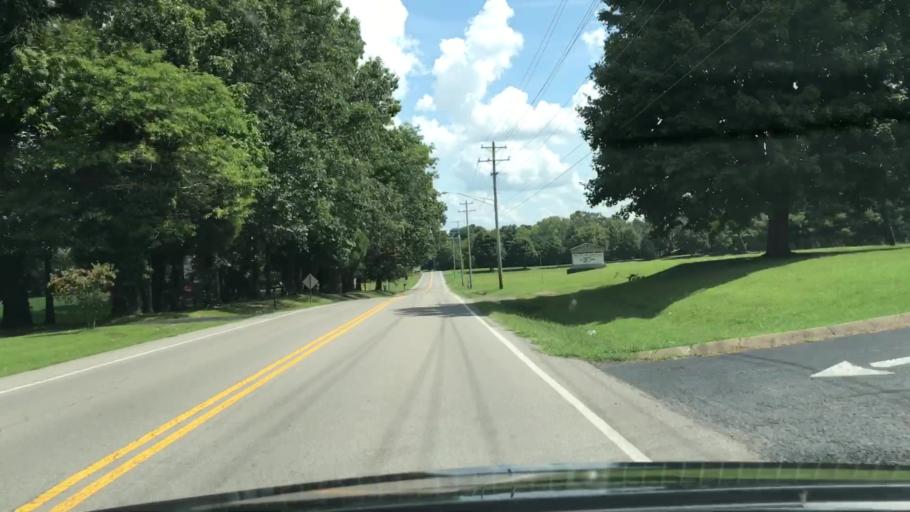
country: US
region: Tennessee
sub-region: Robertson County
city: Cross Plains
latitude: 36.5515
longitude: -86.7374
